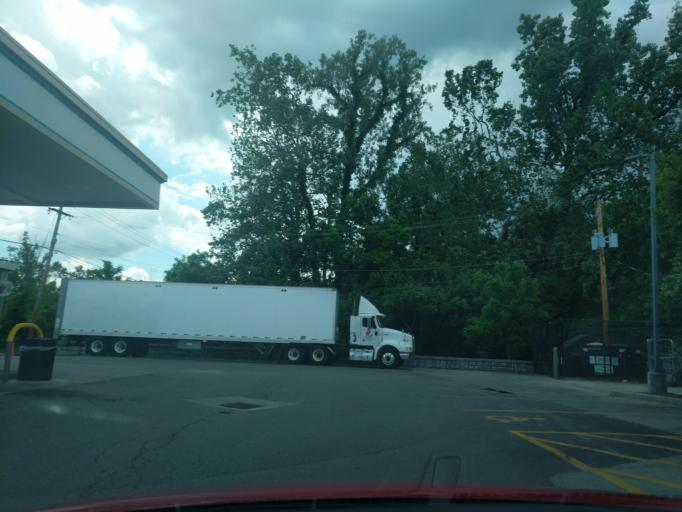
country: US
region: Ohio
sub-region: Franklin County
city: Minerva Park
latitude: 40.0576
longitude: -82.9238
